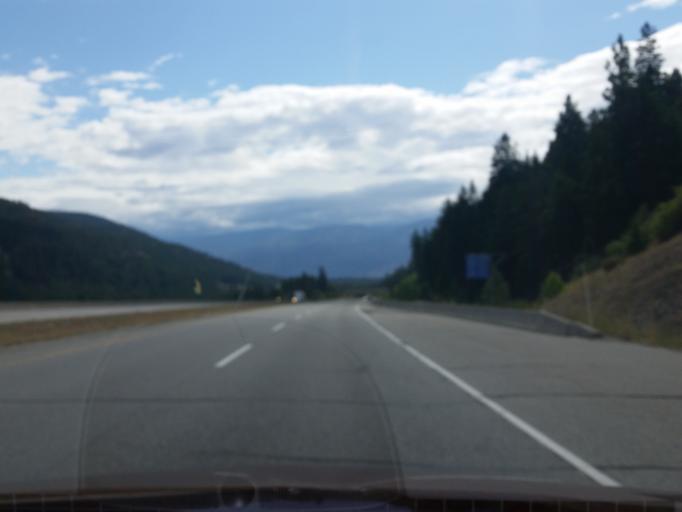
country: CA
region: British Columbia
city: Peachland
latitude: 49.8149
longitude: -119.7657
